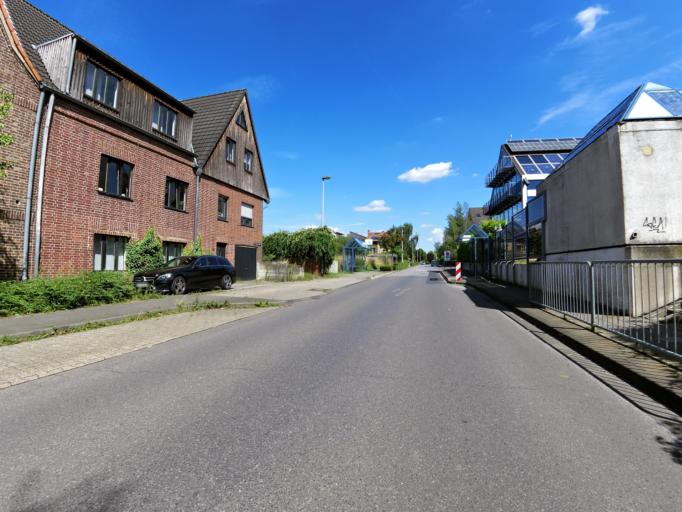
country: NL
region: Limburg
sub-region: Gemeente Kerkrade
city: Kerkrade
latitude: 50.8370
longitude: 6.0706
